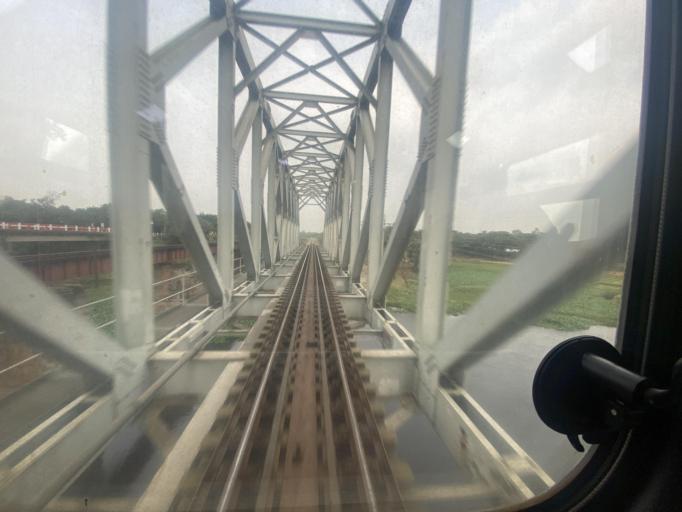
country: BD
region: Dhaka
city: Tungi
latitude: 23.9350
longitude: 90.4902
